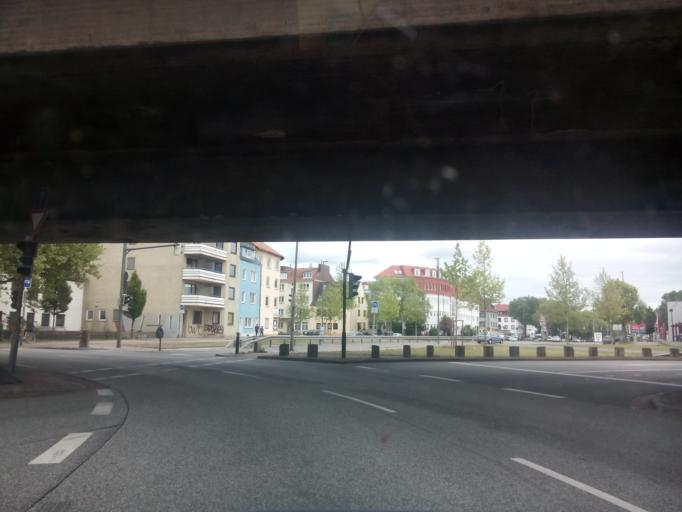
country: DE
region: Bremen
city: Bremen
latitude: 53.0686
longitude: 8.7793
